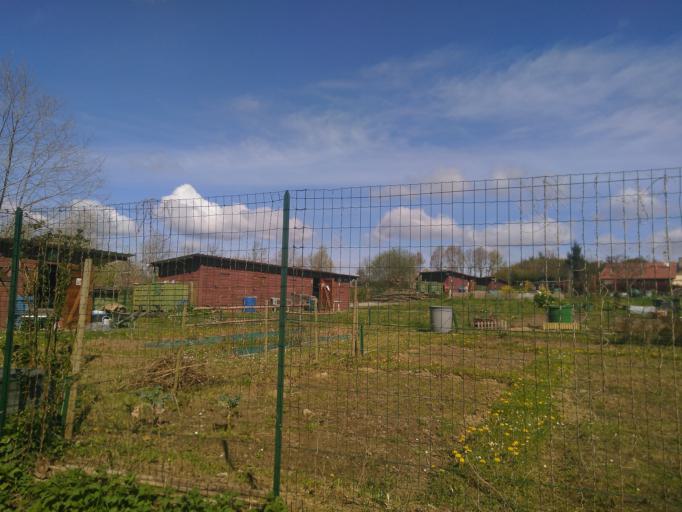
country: FR
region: Aquitaine
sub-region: Departement des Landes
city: Saint-Martin-de-Seignanx
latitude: 43.5371
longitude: -1.3873
